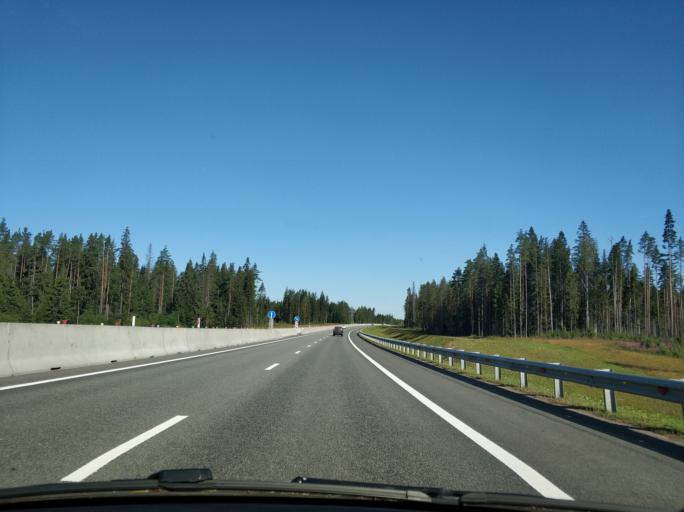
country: RU
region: Leningrad
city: Sosnovo
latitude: 60.5193
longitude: 30.1752
